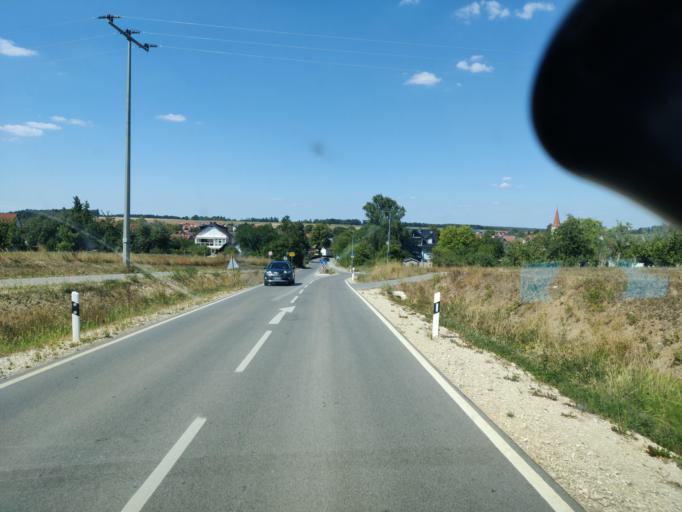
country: DE
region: Bavaria
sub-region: Regierungsbezirk Mittelfranken
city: Thalmassing
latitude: 49.1256
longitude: 11.2118
